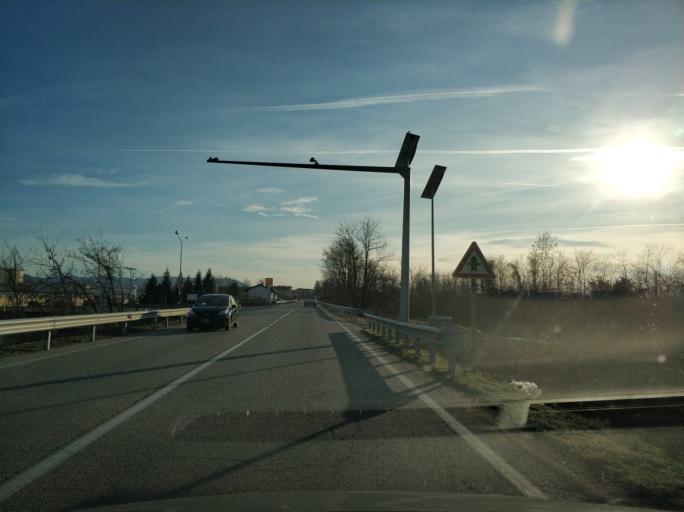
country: IT
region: Piedmont
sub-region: Provincia di Torino
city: Brandizzo
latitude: 45.1841
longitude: 7.8545
